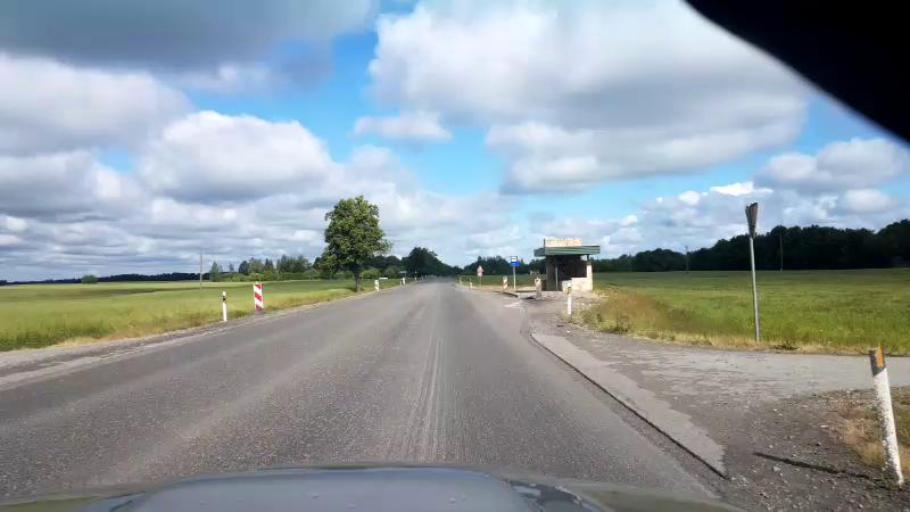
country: LV
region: Bauskas Rajons
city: Bauska
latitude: 56.3228
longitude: 24.3146
